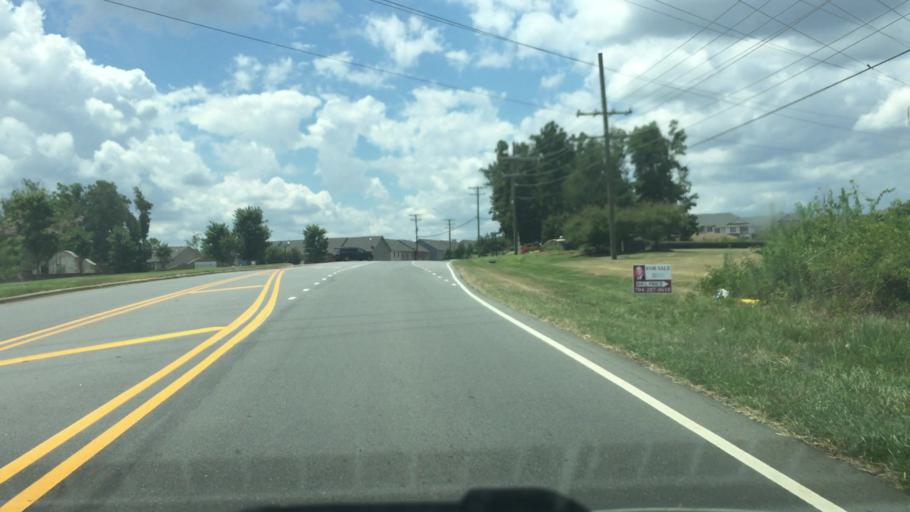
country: US
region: North Carolina
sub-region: Mecklenburg County
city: Huntersville
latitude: 35.4063
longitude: -80.7559
